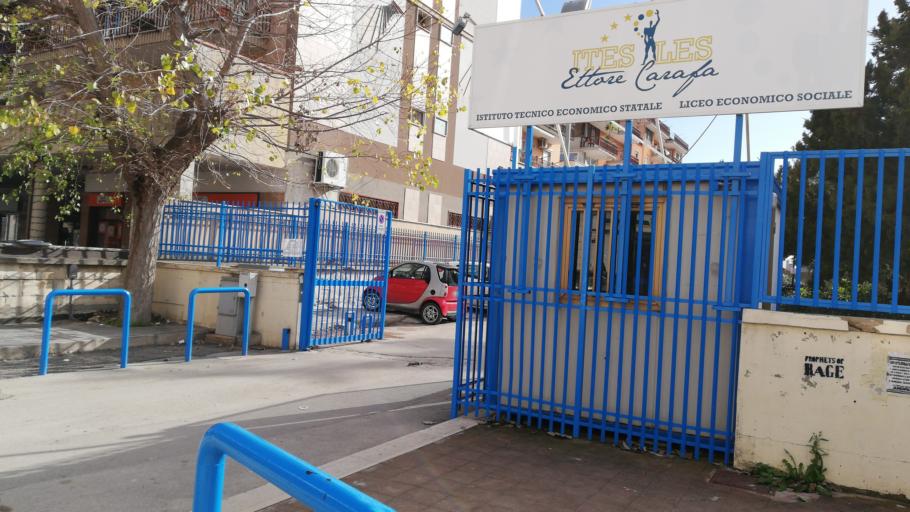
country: IT
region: Apulia
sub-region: Provincia di Barletta - Andria - Trani
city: Andria
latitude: 41.2264
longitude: 16.3099
